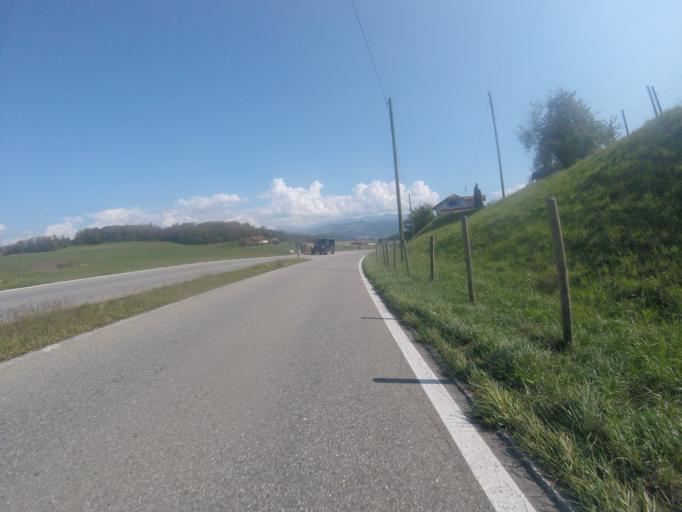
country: CH
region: Bern
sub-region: Thun District
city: Seftigen
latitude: 46.7910
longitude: 7.5569
